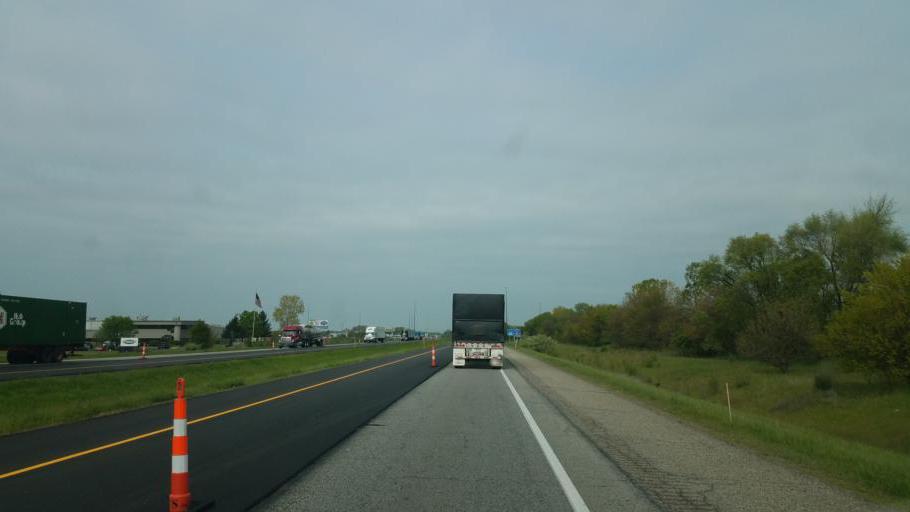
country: US
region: Indiana
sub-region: Elkhart County
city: Simonton Lake
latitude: 41.7319
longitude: -85.9944
